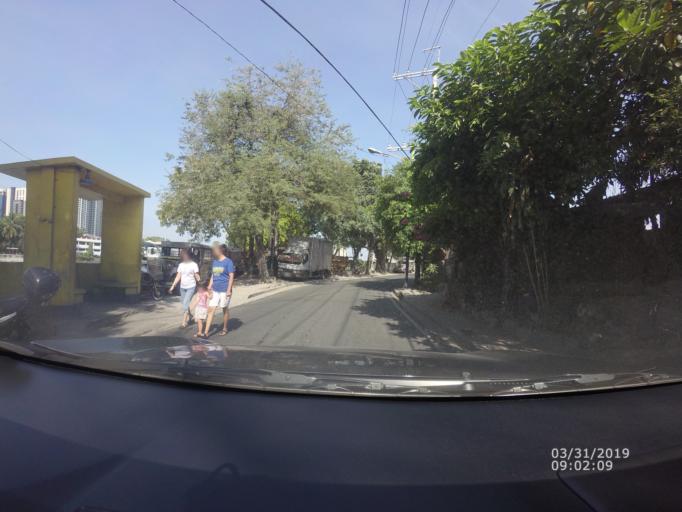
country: PH
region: Metro Manila
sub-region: Mandaluyong
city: Mandaluyong City
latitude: 14.5768
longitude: 121.0232
